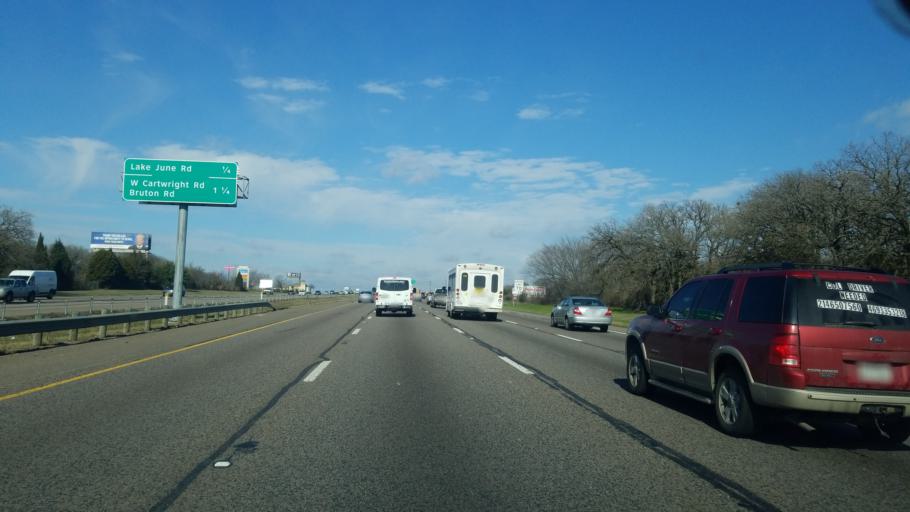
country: US
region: Texas
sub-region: Dallas County
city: Balch Springs
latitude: 32.7275
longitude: -96.6138
